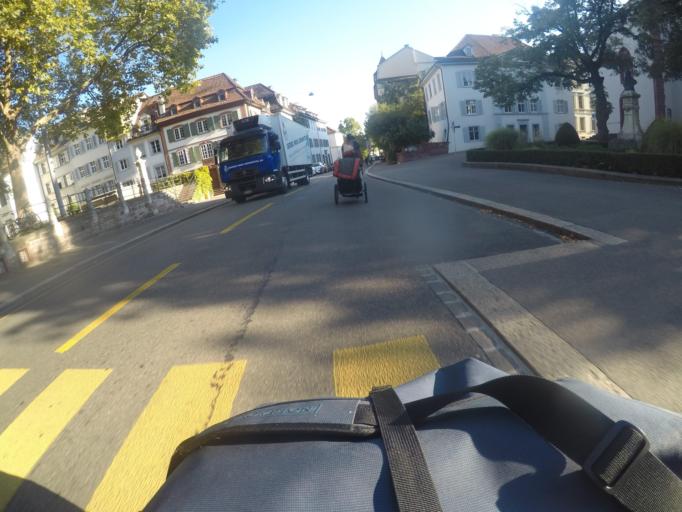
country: CH
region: Basel-City
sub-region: Basel-Stadt
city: Basel
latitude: 47.5592
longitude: 7.5845
